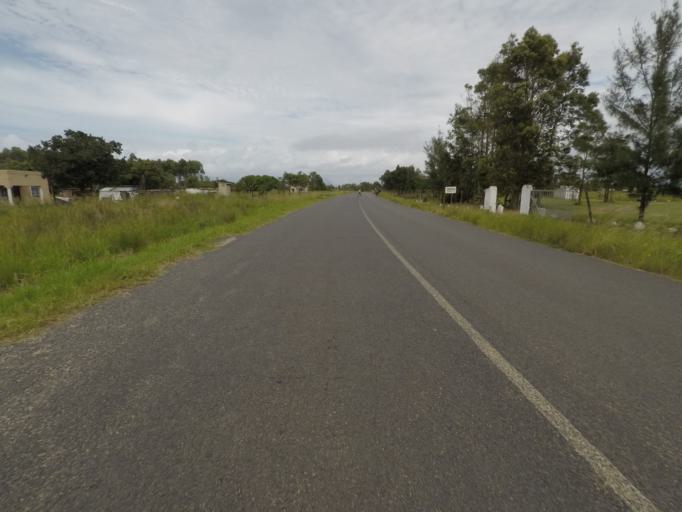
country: ZA
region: KwaZulu-Natal
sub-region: uThungulu District Municipality
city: eSikhawini
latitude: -28.9089
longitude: 31.8803
